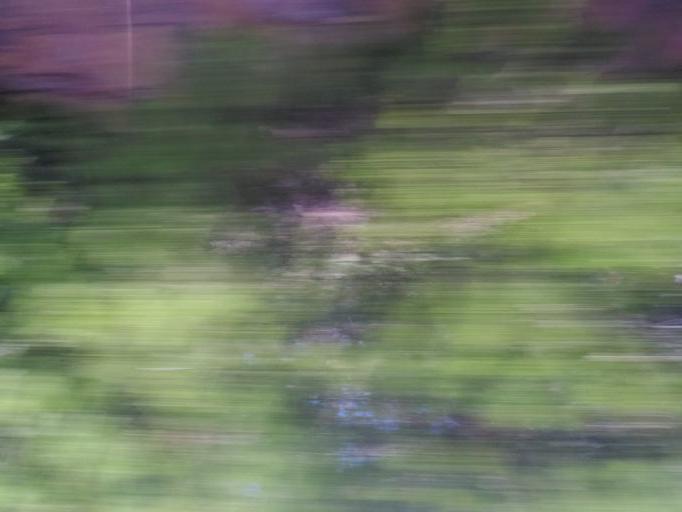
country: GR
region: Crete
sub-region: Nomos Lasithiou
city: Skhisma
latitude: 35.2423
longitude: 25.7296
